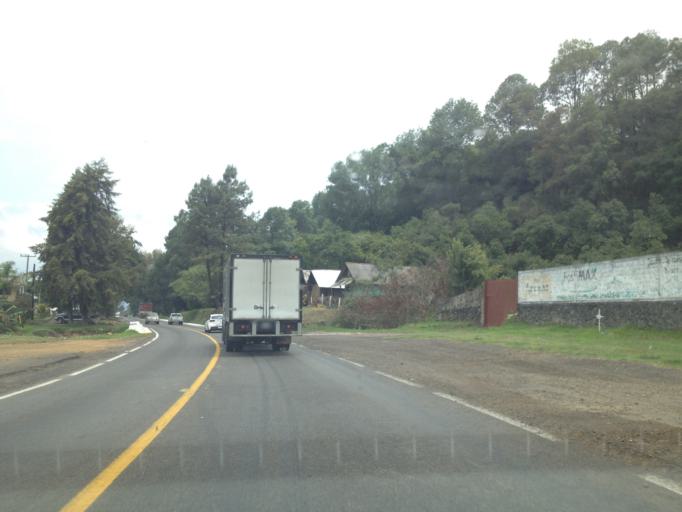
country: MX
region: Michoacan
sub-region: Uruapan
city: Toreo Bajo (El Toreo Bajo)
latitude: 19.4533
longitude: -102.0054
